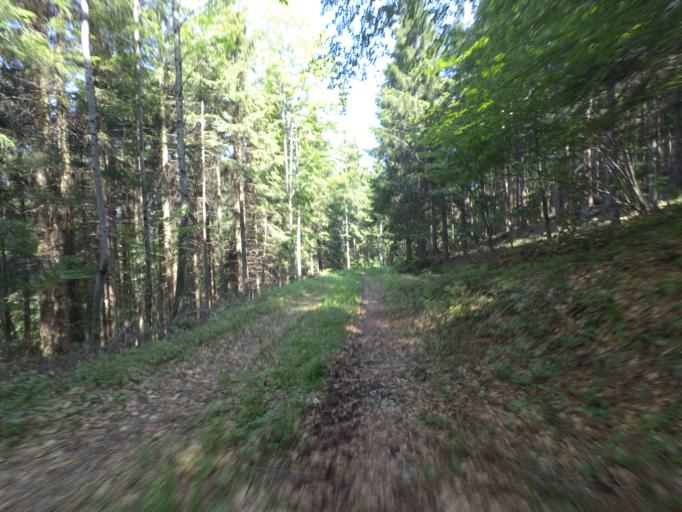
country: AT
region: Salzburg
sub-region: Politischer Bezirk Salzburg-Umgebung
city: Koppl
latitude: 47.7838
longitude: 13.1323
